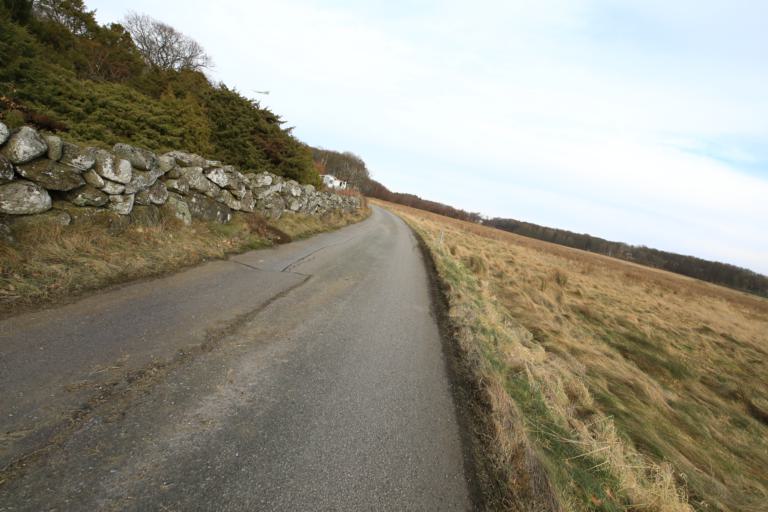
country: SE
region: Halland
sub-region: Varbergs Kommun
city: Varberg
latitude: 57.1924
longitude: 12.2026
